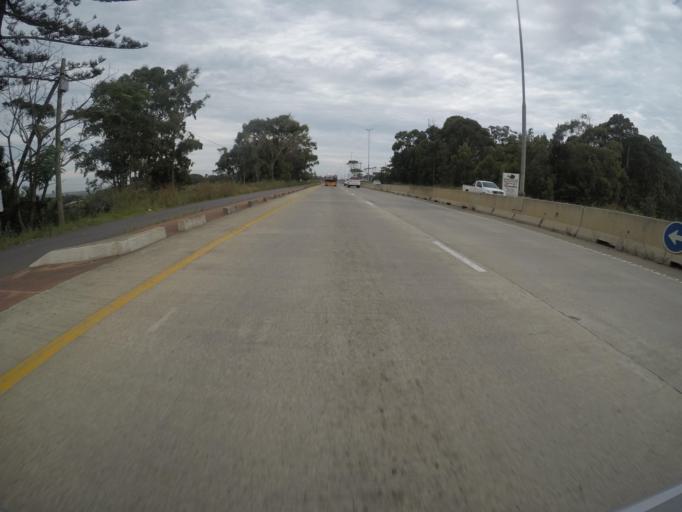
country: ZA
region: Eastern Cape
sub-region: Buffalo City Metropolitan Municipality
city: East London
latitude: -32.9383
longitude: 27.9798
